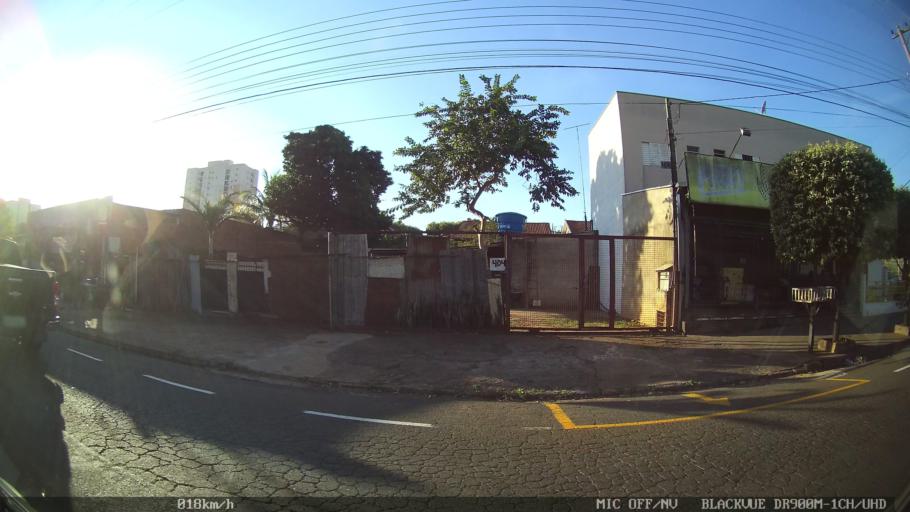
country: BR
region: Sao Paulo
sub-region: Sao Jose Do Rio Preto
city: Sao Jose do Rio Preto
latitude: -20.7869
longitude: -49.3658
